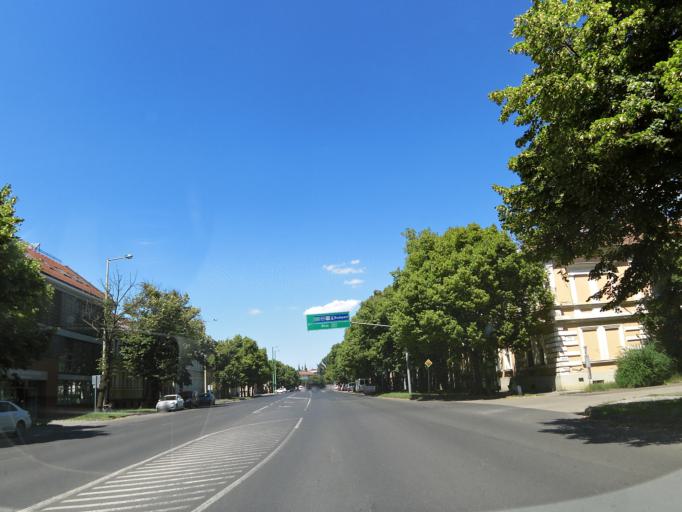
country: HU
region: Csongrad
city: Szeged
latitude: 46.2504
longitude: 20.1383
